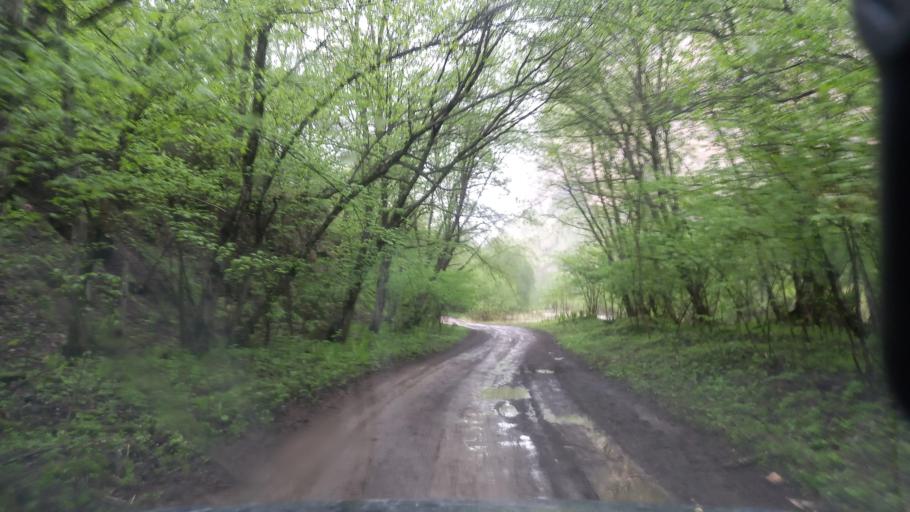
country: RU
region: Kabardino-Balkariya
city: Bylym
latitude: 43.5914
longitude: 42.9871
